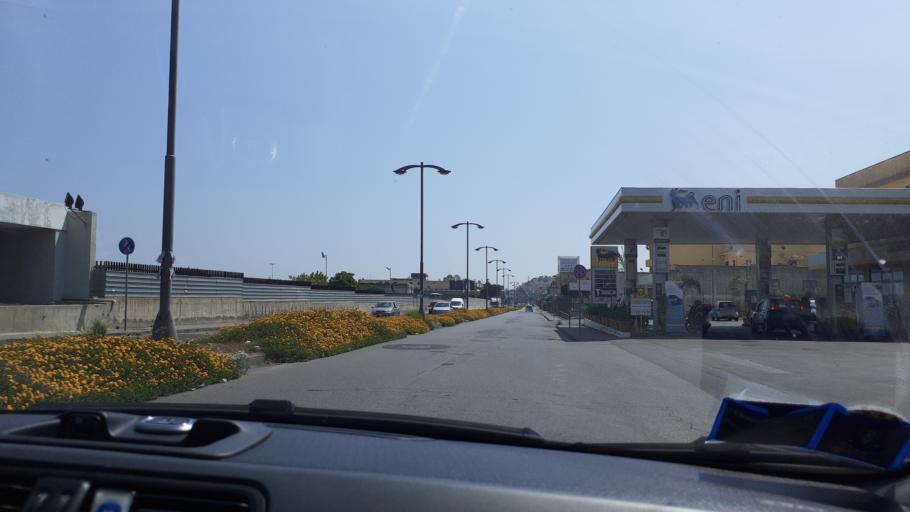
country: IT
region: Sicily
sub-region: Catania
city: Misterbianco
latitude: 37.5146
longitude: 15.0240
